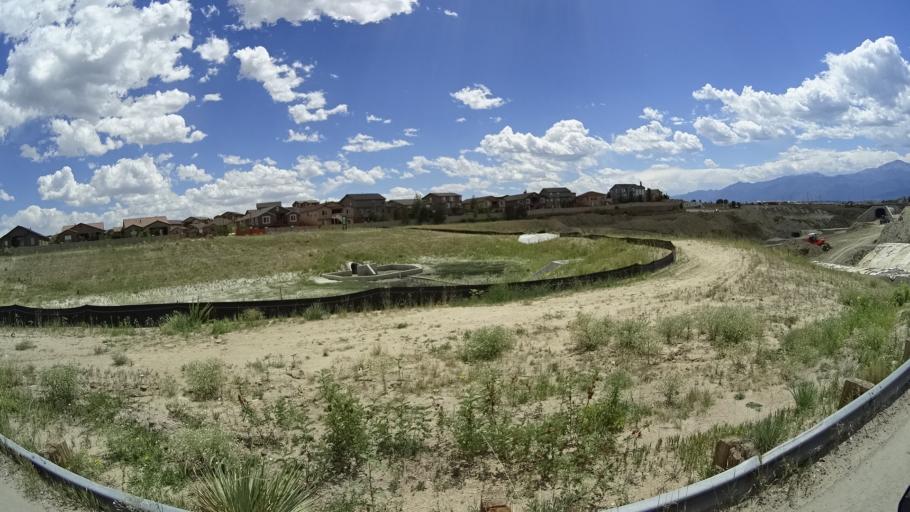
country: US
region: Colorado
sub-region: El Paso County
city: Black Forest
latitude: 38.9513
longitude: -104.7126
